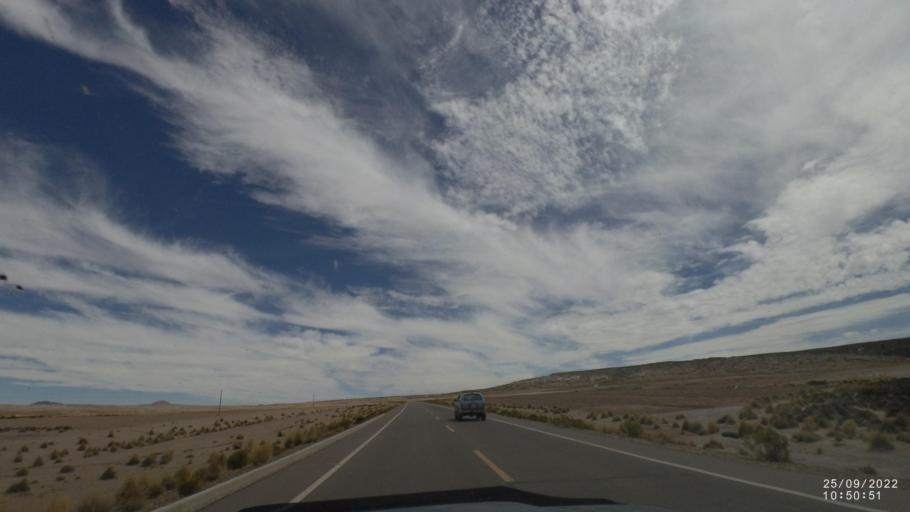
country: BO
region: Oruro
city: Challapata
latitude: -19.5698
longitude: -66.8419
